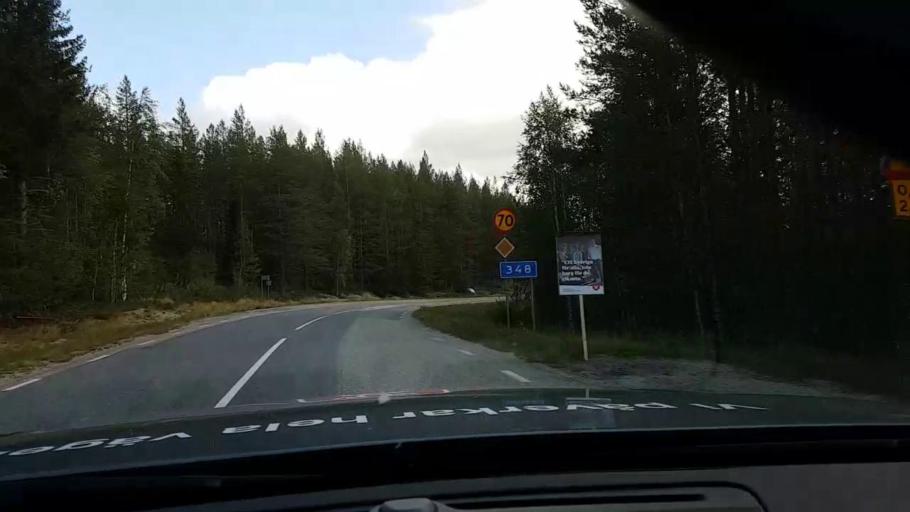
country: SE
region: Vaesterbotten
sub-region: Asele Kommun
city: Asele
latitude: 63.7963
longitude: 17.5646
